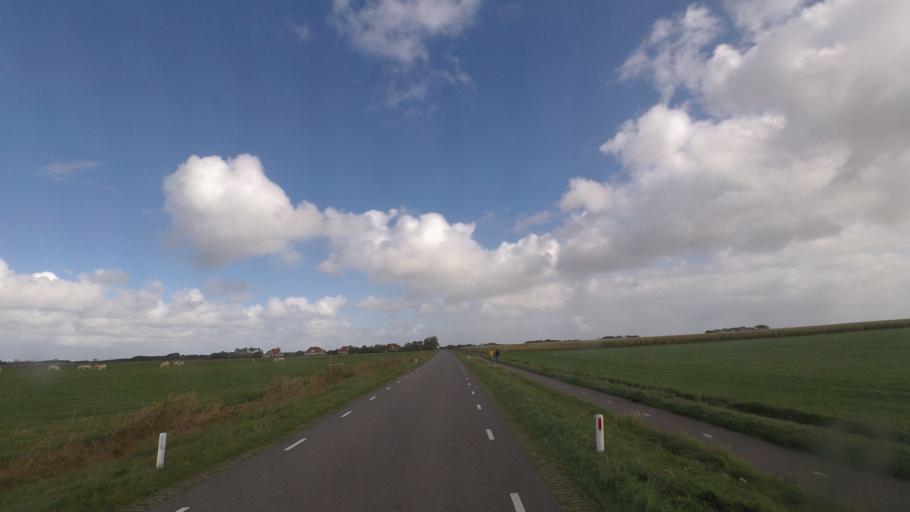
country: NL
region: Friesland
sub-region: Gemeente Ameland
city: Hollum
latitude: 53.4376
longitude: 5.6487
